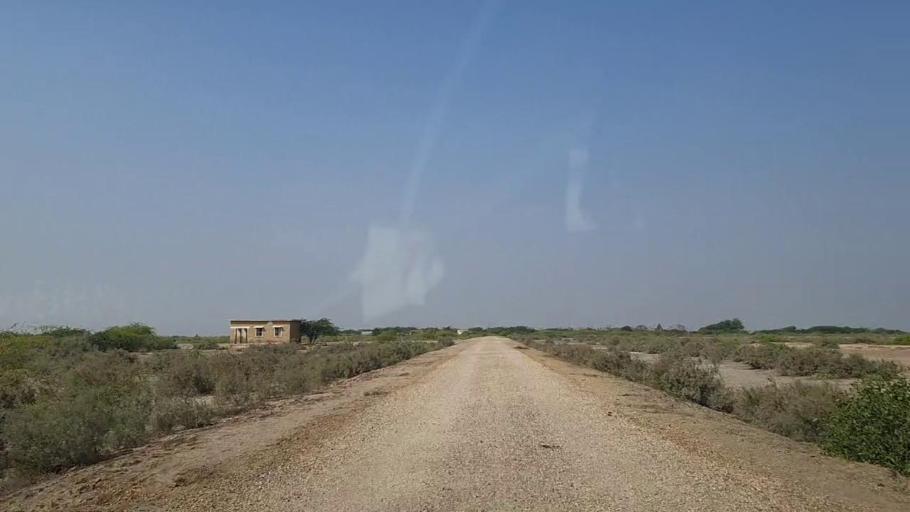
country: PK
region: Sindh
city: Mirpur Sakro
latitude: 24.6587
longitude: 67.7267
